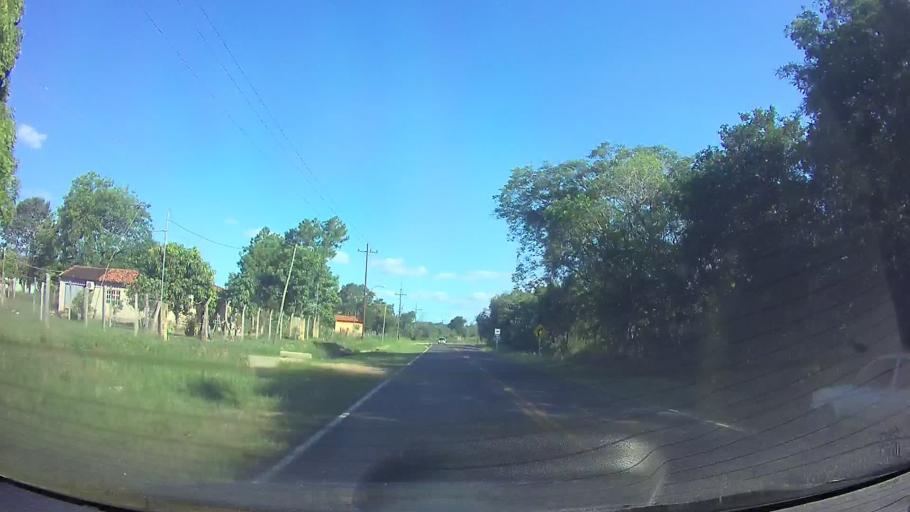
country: PY
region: Cordillera
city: Atyra
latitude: -25.2943
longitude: -57.1645
